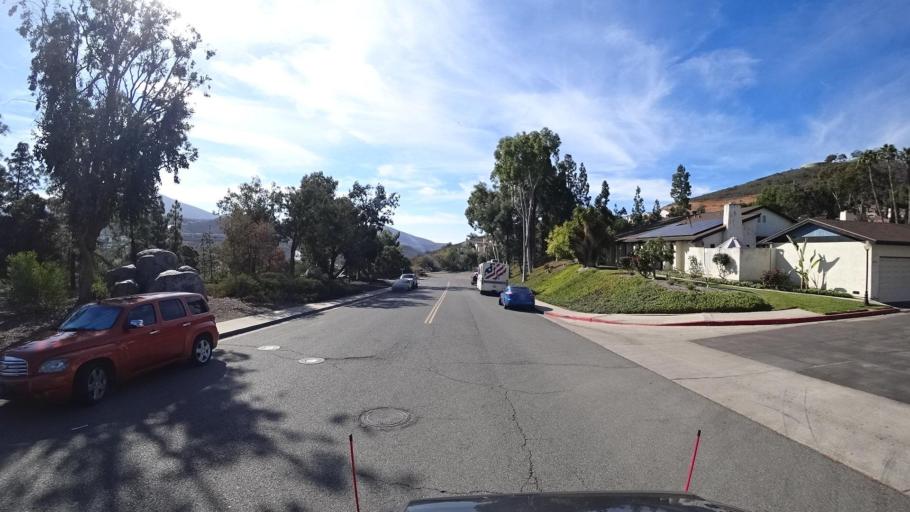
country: US
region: California
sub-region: San Diego County
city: Spring Valley
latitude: 32.7291
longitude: -116.9739
